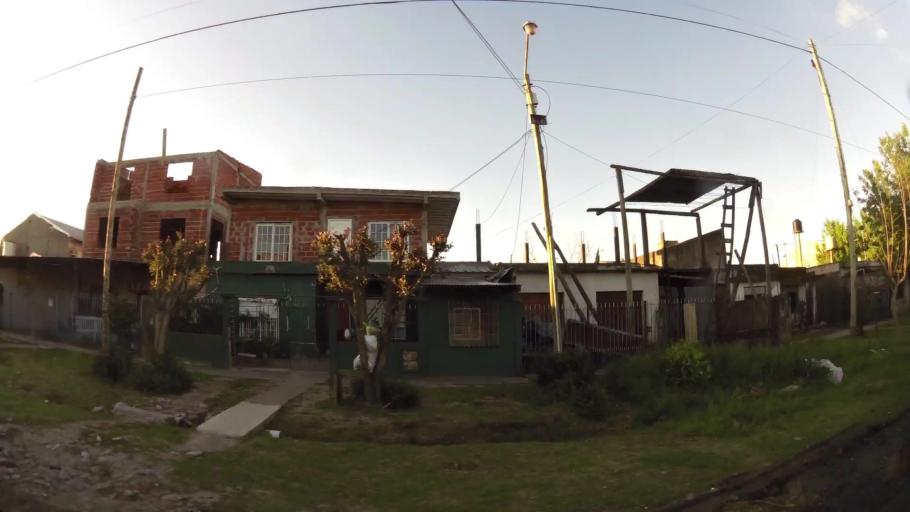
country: AR
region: Buenos Aires
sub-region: Partido de Almirante Brown
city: Adrogue
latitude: -34.7834
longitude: -58.3350
